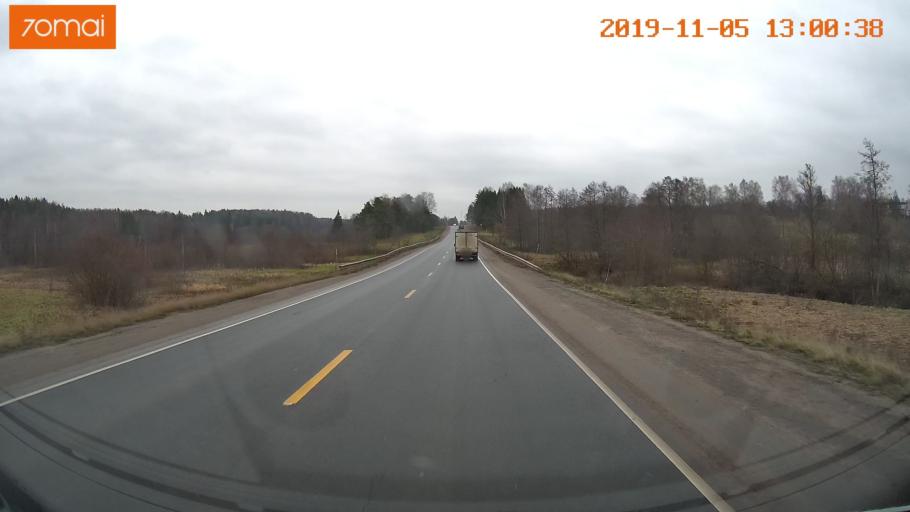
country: RU
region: Ivanovo
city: Kokhma
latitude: 56.9130
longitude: 41.1484
